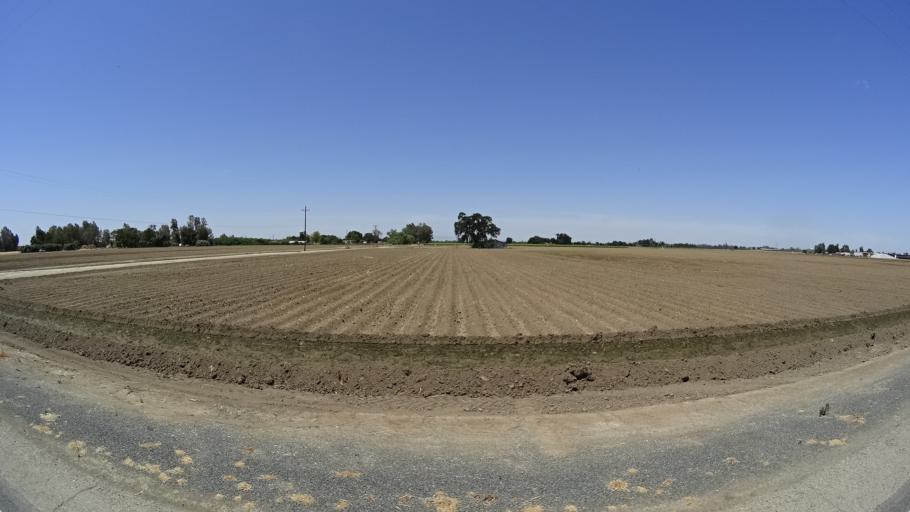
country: US
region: California
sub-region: Kings County
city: Lemoore
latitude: 36.3446
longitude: -119.7808
